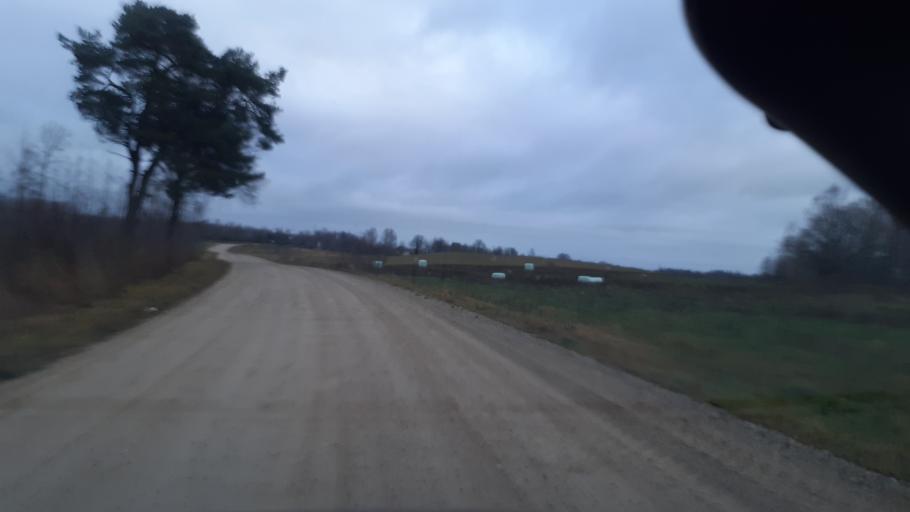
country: LV
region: Alsunga
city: Alsunga
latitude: 56.8960
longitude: 21.7074
